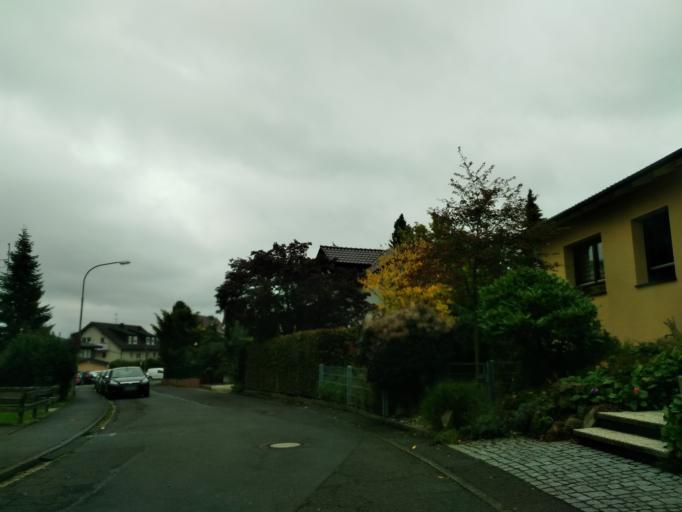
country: DE
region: Rheinland-Pfalz
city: Windhagen
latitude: 50.6585
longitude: 7.3006
